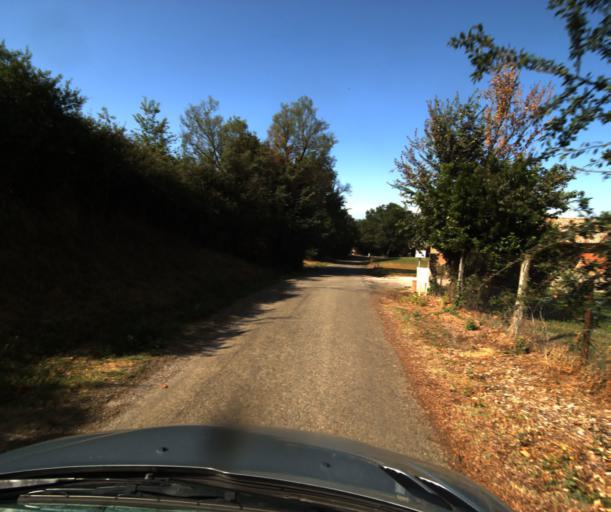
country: FR
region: Midi-Pyrenees
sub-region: Departement du Tarn-et-Garonne
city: Finhan
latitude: 43.9137
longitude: 1.2653
